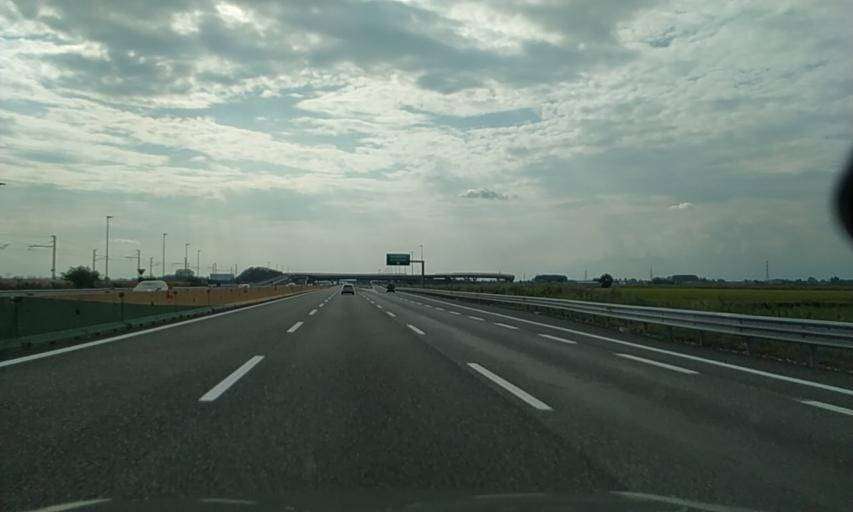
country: IT
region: Piedmont
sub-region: Provincia di Novara
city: Casaleggio Novara
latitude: 45.4680
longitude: 8.4847
